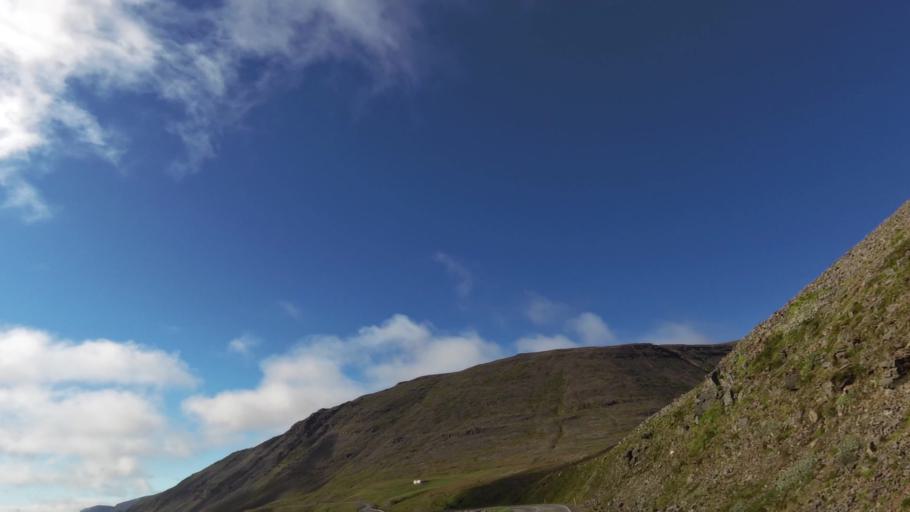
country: IS
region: West
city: Olafsvik
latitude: 65.5480
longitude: -23.8880
